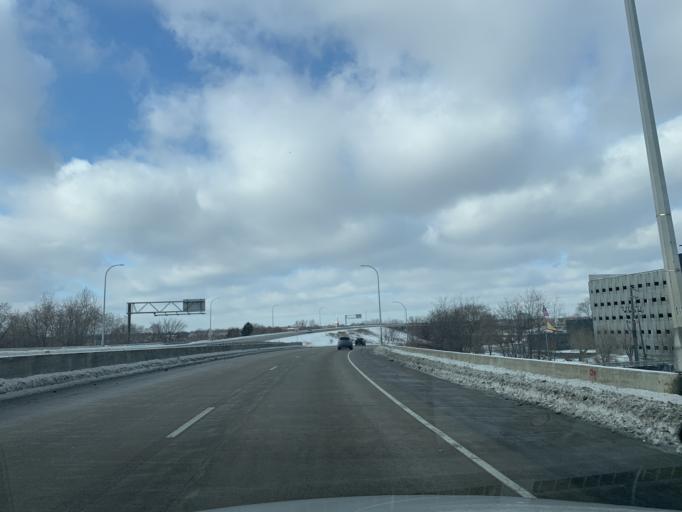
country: US
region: Minnesota
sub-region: Hennepin County
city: Minneapolis
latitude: 44.9881
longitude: -93.2825
